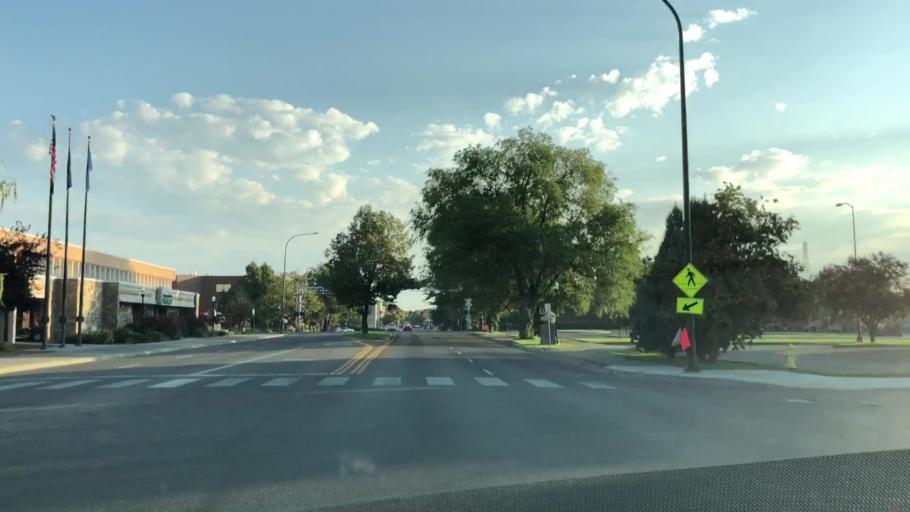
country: US
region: Idaho
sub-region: Bonneville County
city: Idaho Falls
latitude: 43.4903
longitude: -112.0441
